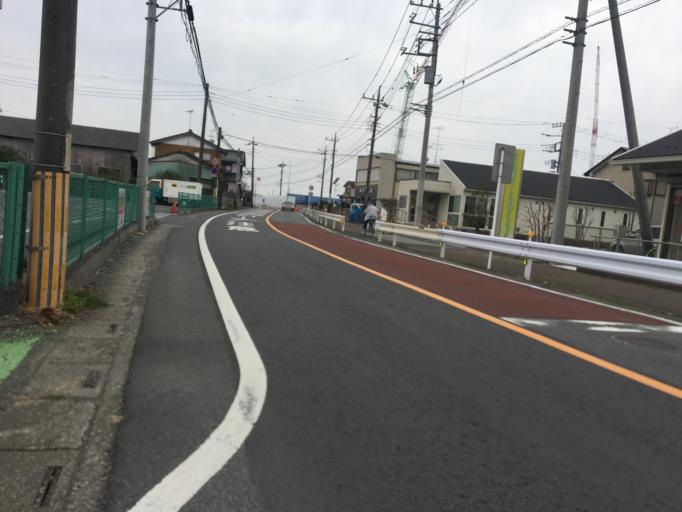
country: JP
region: Saitama
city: Kazo
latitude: 36.1191
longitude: 139.5973
